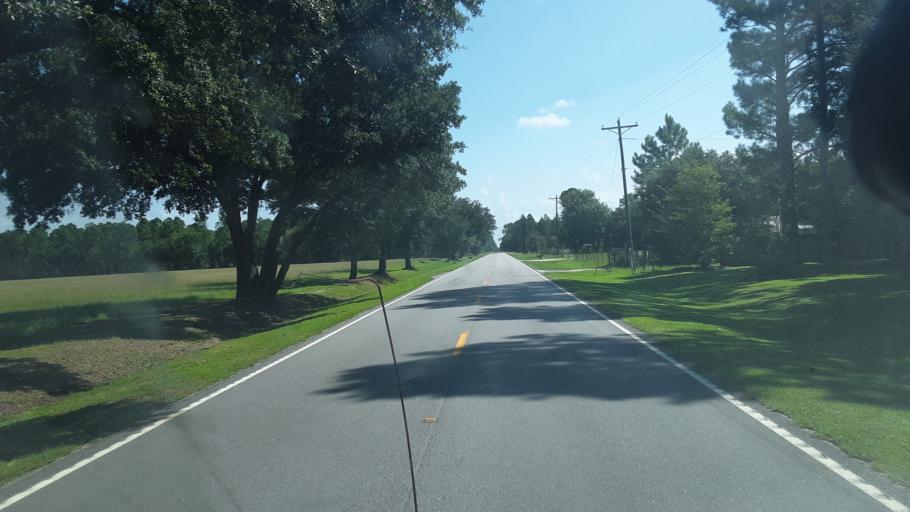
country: US
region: South Carolina
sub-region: Hampton County
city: Varnville
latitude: 32.8691
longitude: -81.0570
